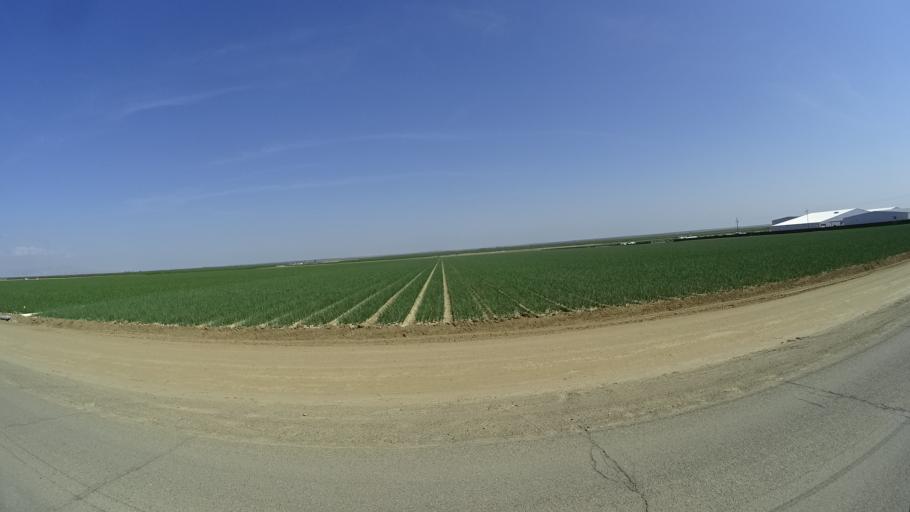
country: US
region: California
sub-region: Kings County
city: Avenal
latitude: 36.0725
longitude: -120.0503
